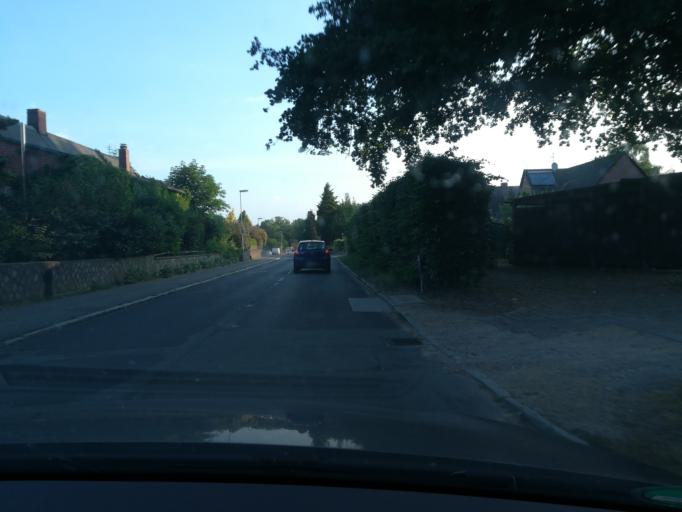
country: DE
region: Schleswig-Holstein
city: Grossensee
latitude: 53.6120
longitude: 10.3418
